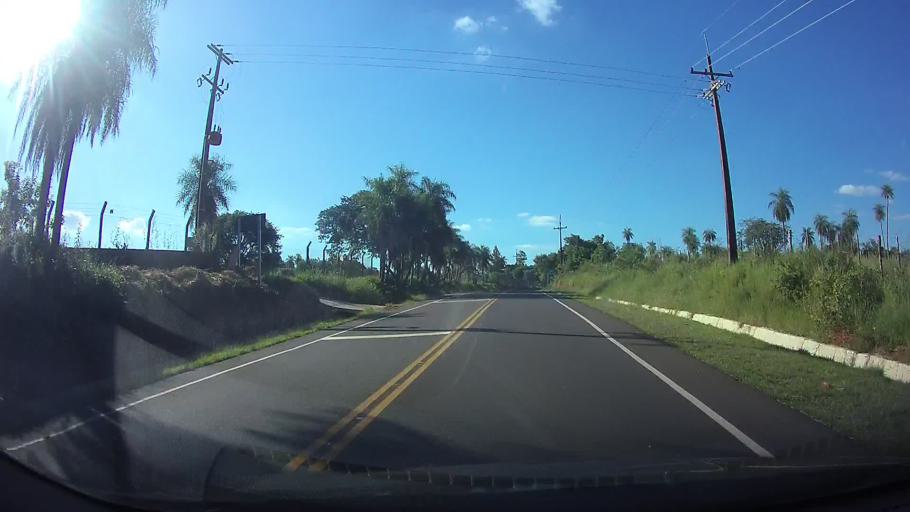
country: PY
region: Cordillera
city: Caacupe
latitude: -25.3539
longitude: -57.1485
